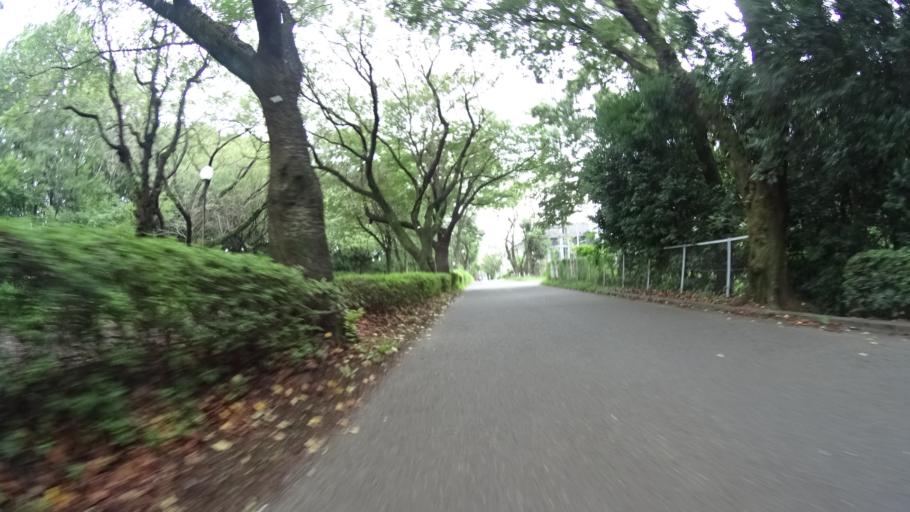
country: JP
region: Tokyo
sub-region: Machida-shi
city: Machida
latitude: 35.5865
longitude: 139.4028
